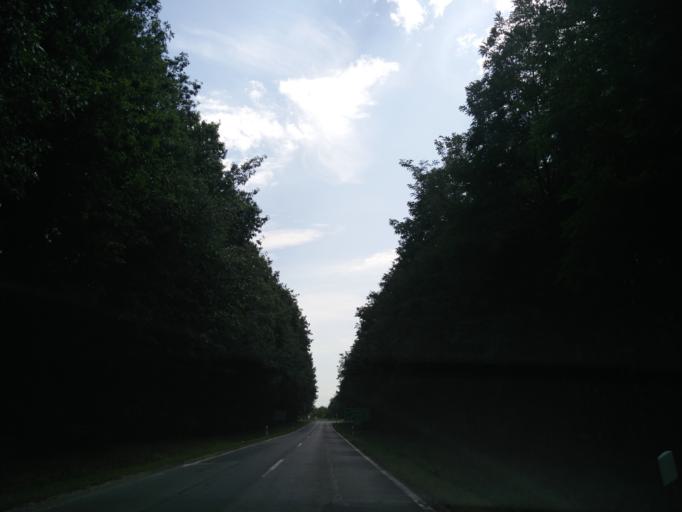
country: HU
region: Zala
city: Zalaegerszeg
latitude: 46.8789
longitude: 16.8532
